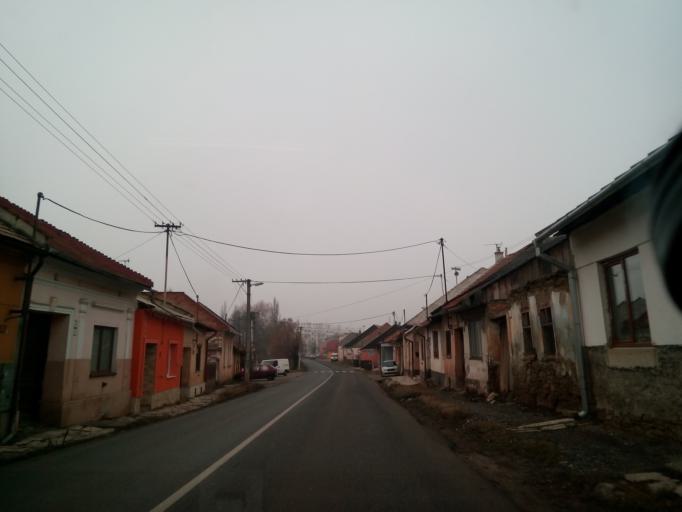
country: SK
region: Presovsky
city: Spisske Podhradie
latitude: 48.9477
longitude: 20.8013
